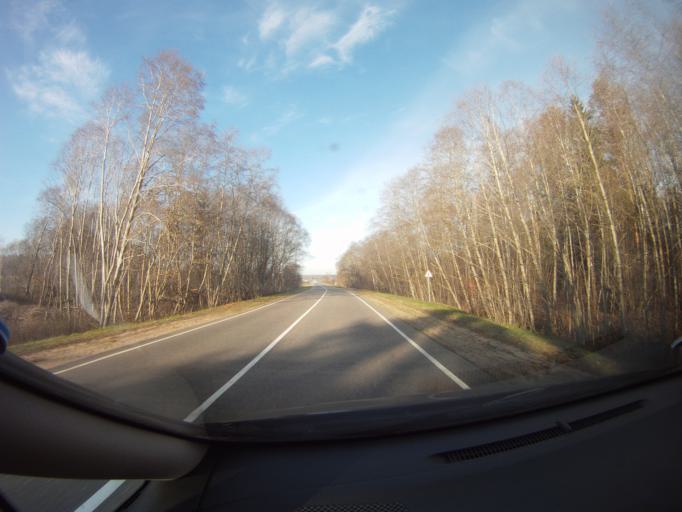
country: BY
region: Minsk
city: Il'ya
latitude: 54.4727
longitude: 27.2727
